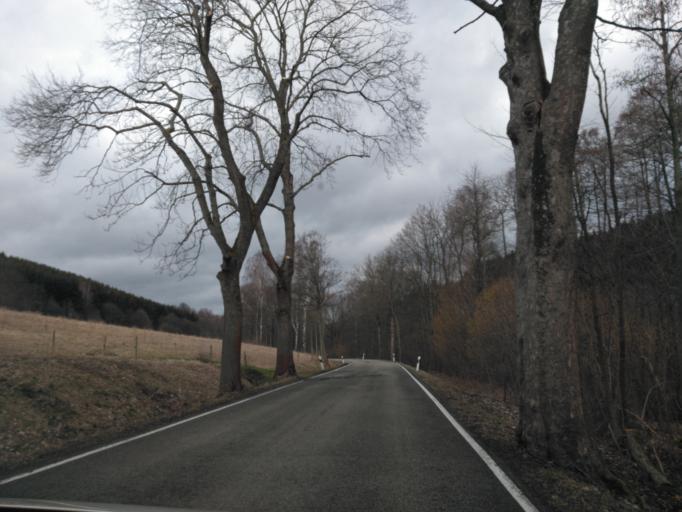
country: DE
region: Saxony
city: Konigswalde
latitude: 50.5808
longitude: 13.0502
